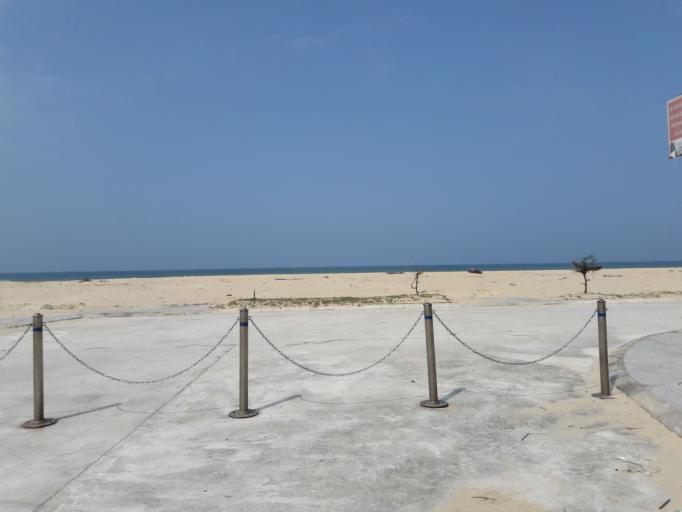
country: VN
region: Thua Thien-Hue
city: Hue
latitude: 16.5578
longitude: 107.6558
